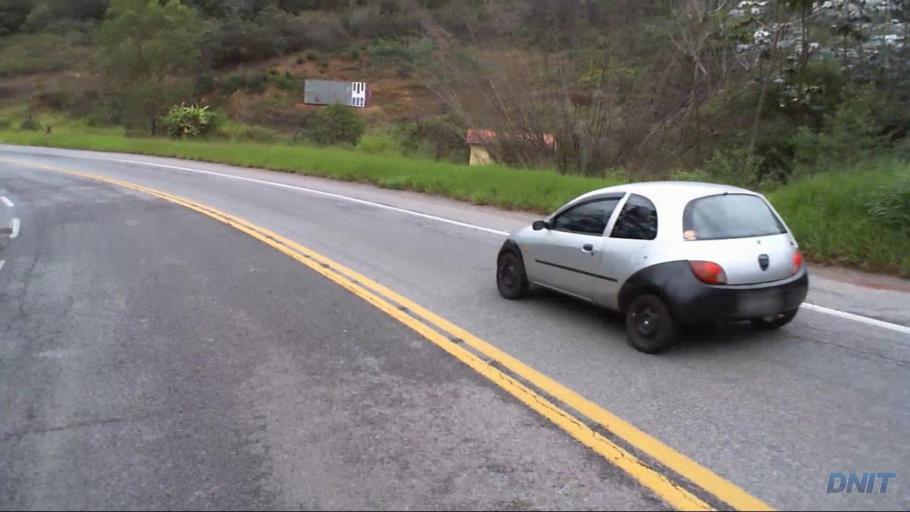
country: BR
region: Minas Gerais
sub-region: Joao Monlevade
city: Joao Monlevade
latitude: -19.8518
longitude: -43.2727
